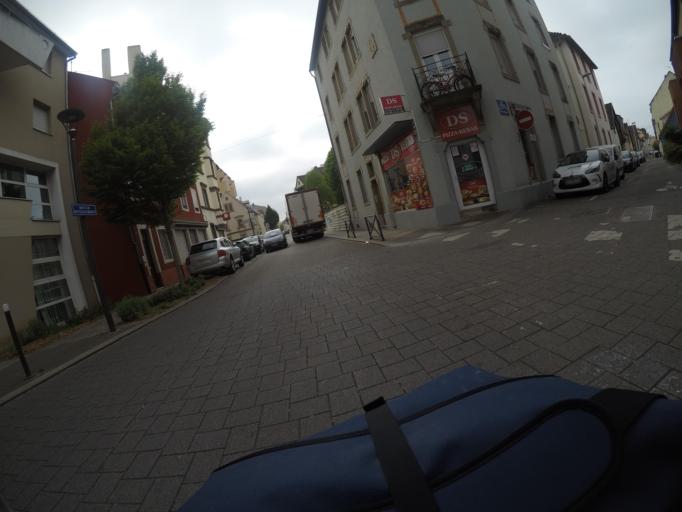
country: FR
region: Alsace
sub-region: Departement du Bas-Rhin
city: Strasbourg
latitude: 48.5949
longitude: 7.7185
